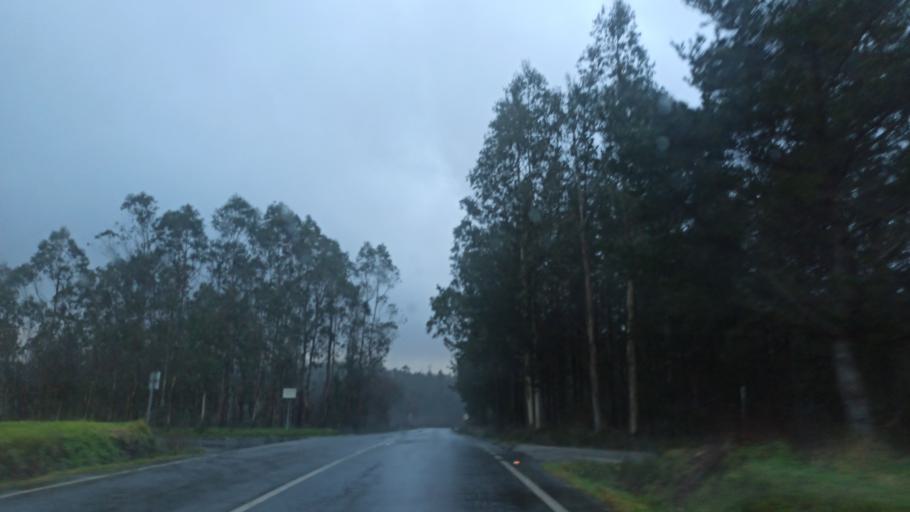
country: ES
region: Galicia
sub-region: Provincia da Coruna
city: Santa Comba
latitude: 43.0560
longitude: -8.7519
